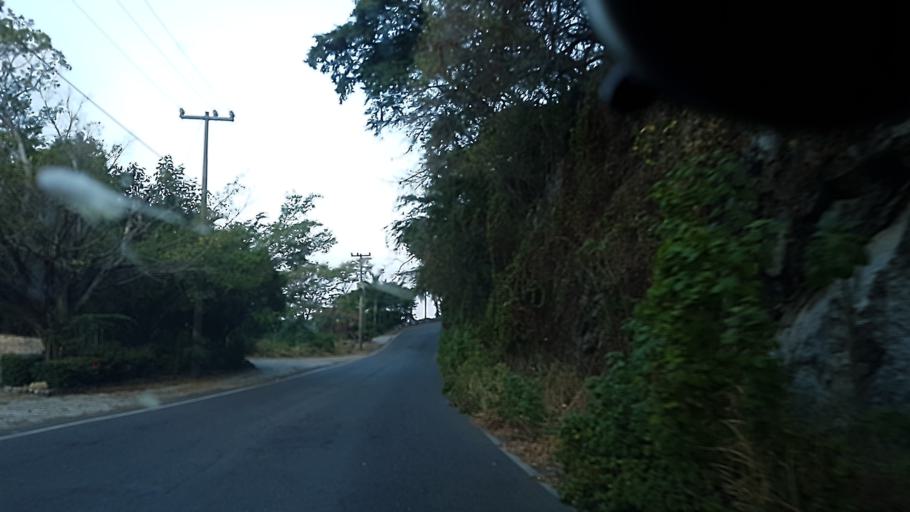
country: MX
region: Jalisco
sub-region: Puerto Vallarta
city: Puerto Vallarta
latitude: 20.5167
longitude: -105.3183
